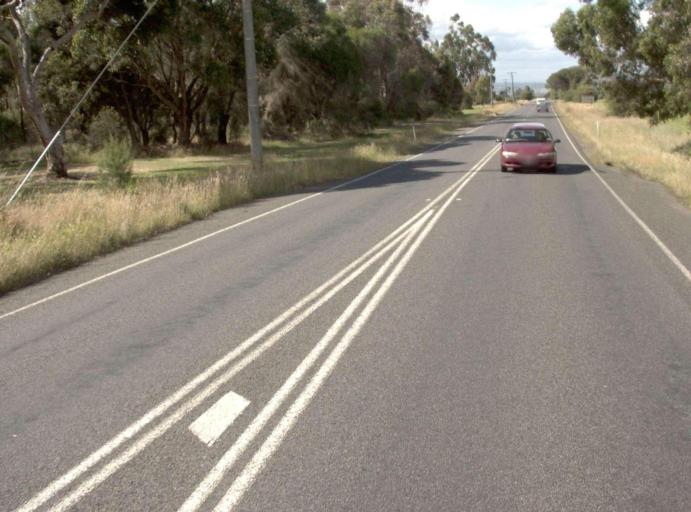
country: AU
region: Victoria
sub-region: Latrobe
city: Morwell
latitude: -38.2785
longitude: 146.4321
